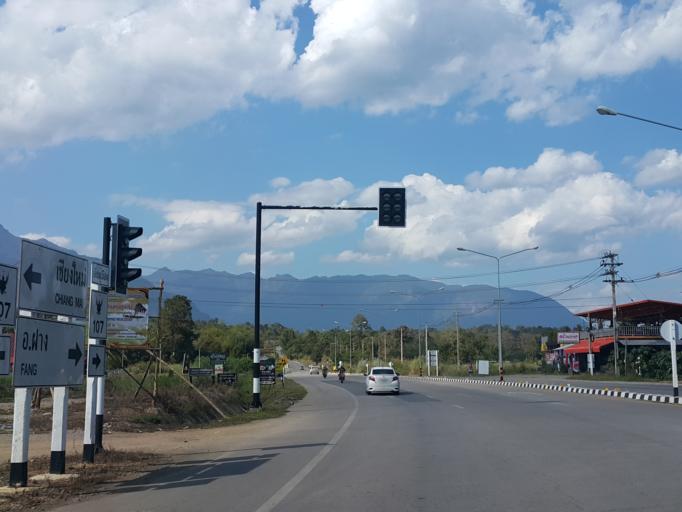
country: TH
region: Chiang Mai
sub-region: Amphoe Chiang Dao
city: Chiang Dao
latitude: 19.3482
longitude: 98.9606
